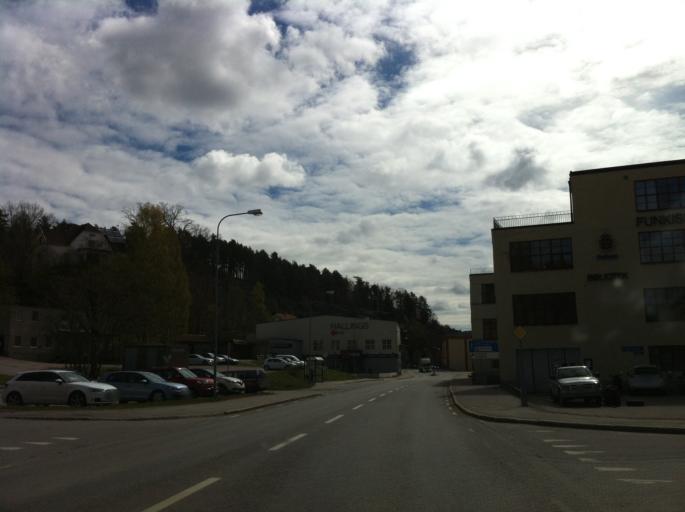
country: SE
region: OEstergoetland
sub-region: Valdemarsviks Kommun
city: Valdemarsvik
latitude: 58.1788
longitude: 16.6652
